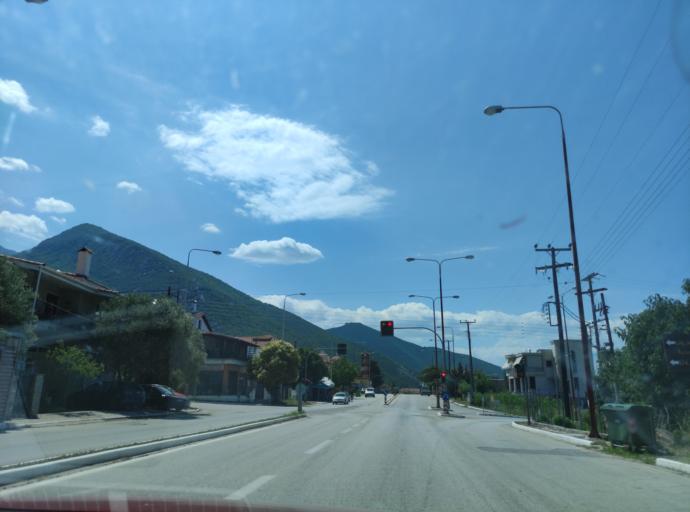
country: GR
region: East Macedonia and Thrace
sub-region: Nomos Kavalas
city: Nikisiani
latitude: 40.9711
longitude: 24.1500
